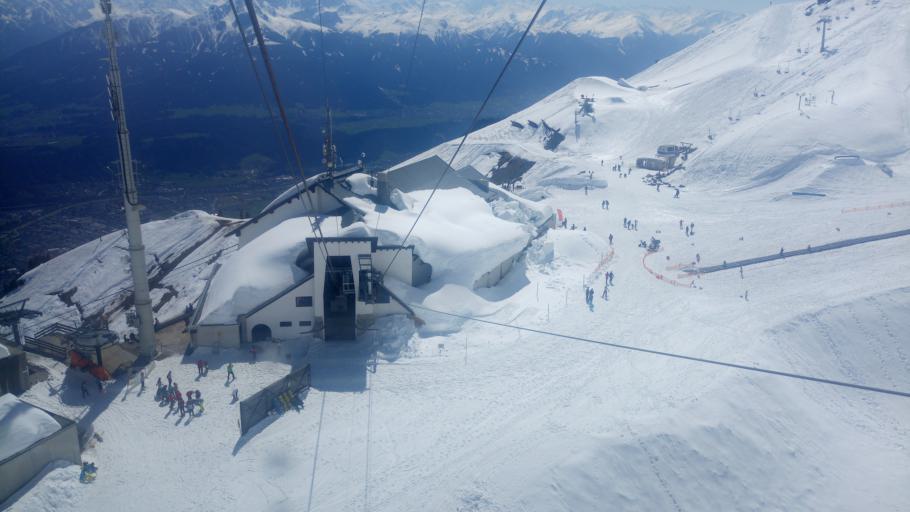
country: AT
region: Tyrol
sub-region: Innsbruck Stadt
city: Innsbruck
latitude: 47.3075
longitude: 11.3805
